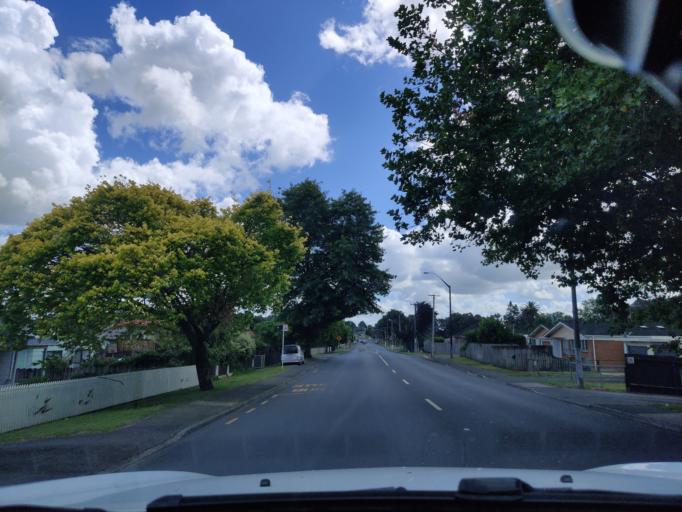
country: NZ
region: Auckland
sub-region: Auckland
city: Papakura
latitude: -37.0689
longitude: 174.9482
